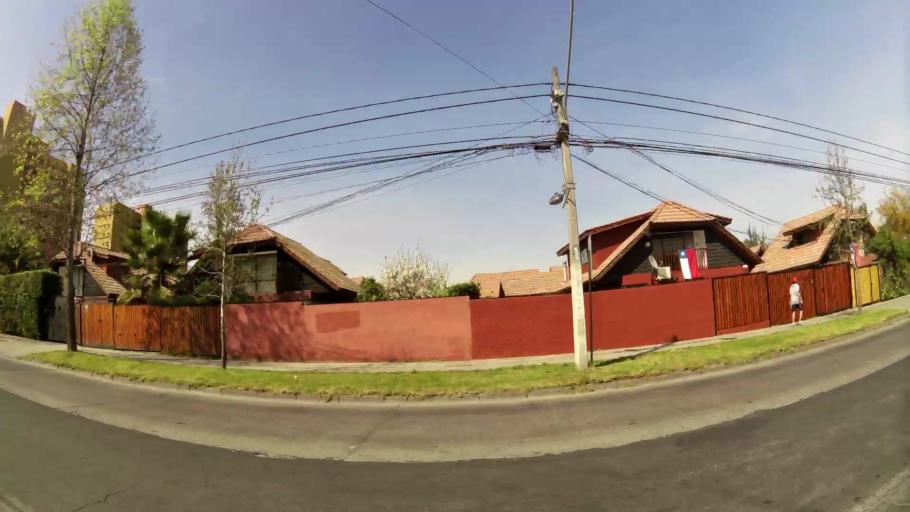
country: CL
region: Santiago Metropolitan
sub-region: Provincia de Santiago
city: Villa Presidente Frei, Nunoa, Santiago, Chile
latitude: -33.5224
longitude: -70.5662
